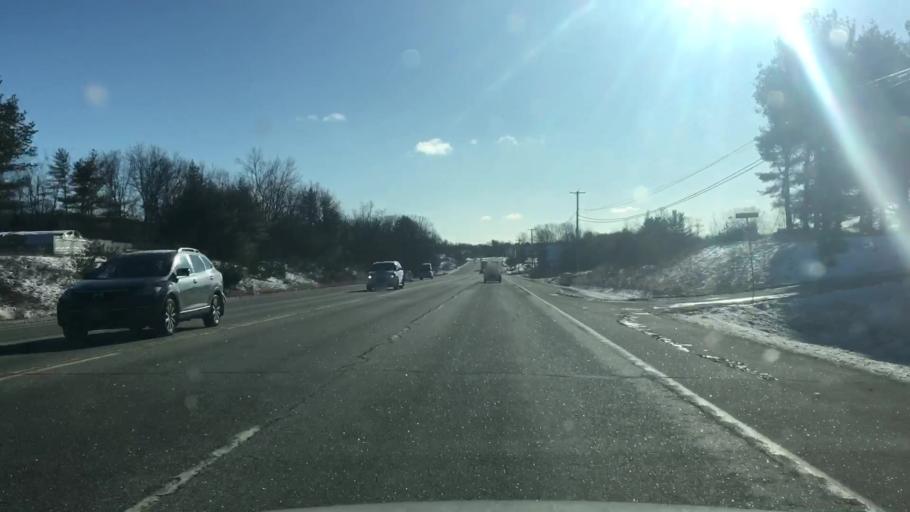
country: US
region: Maine
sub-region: Androscoggin County
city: Lewiston
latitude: 44.1675
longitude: -70.2330
